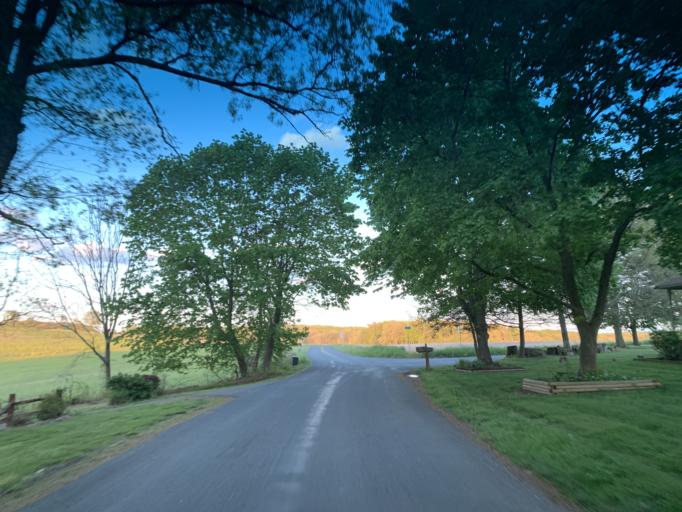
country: US
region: Maryland
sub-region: Harford County
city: Jarrettsville
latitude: 39.6586
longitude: -76.4170
